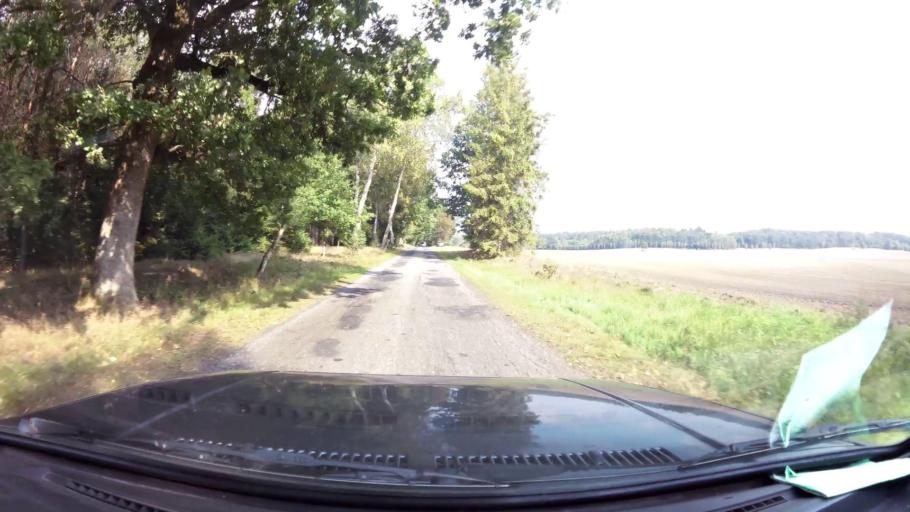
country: PL
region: West Pomeranian Voivodeship
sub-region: Powiat koszalinski
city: Bobolice
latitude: 54.0914
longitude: 16.4853
